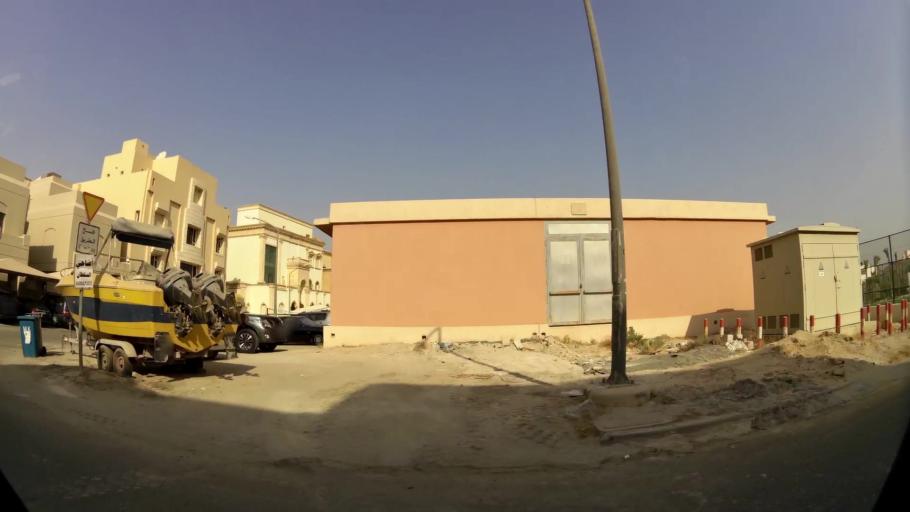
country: KW
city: Bayan
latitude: 29.2817
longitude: 48.0432
